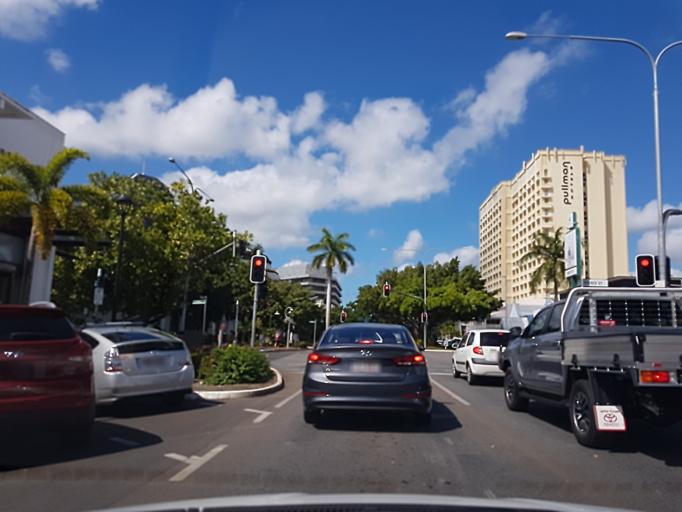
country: AU
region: Queensland
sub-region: Cairns
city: Cairns
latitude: -16.9227
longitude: 145.7781
